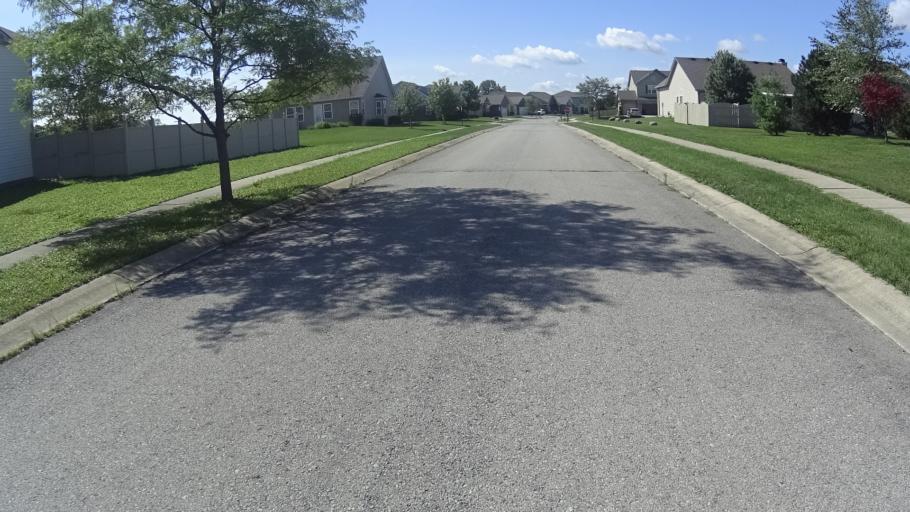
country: US
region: Indiana
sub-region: Madison County
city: Pendleton
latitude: 39.9821
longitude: -85.7431
